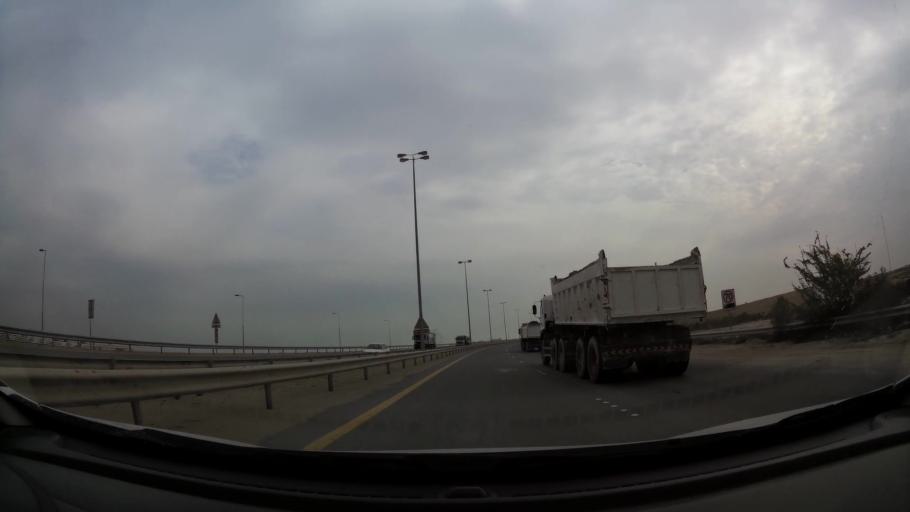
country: BH
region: Northern
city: Sitrah
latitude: 26.0728
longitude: 50.6150
